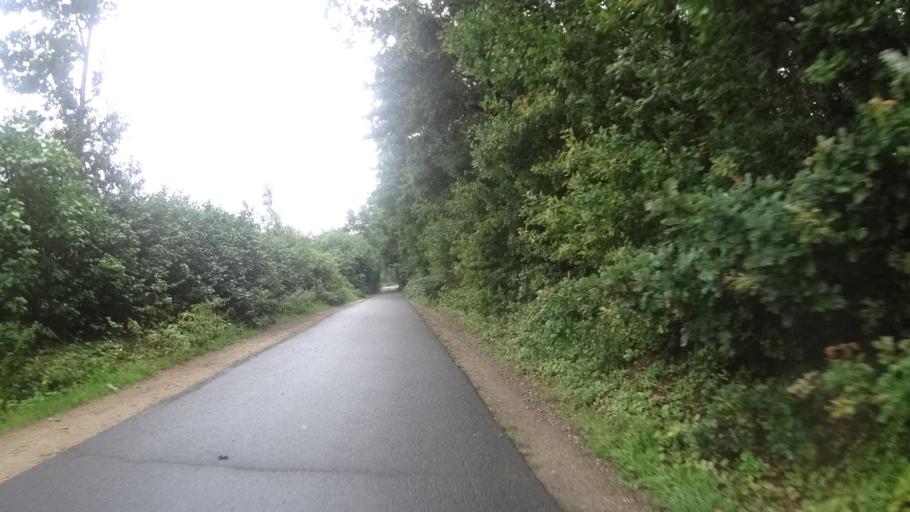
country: DE
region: Schleswig-Holstein
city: Siebeneichen
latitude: 53.5151
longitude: 10.6224
